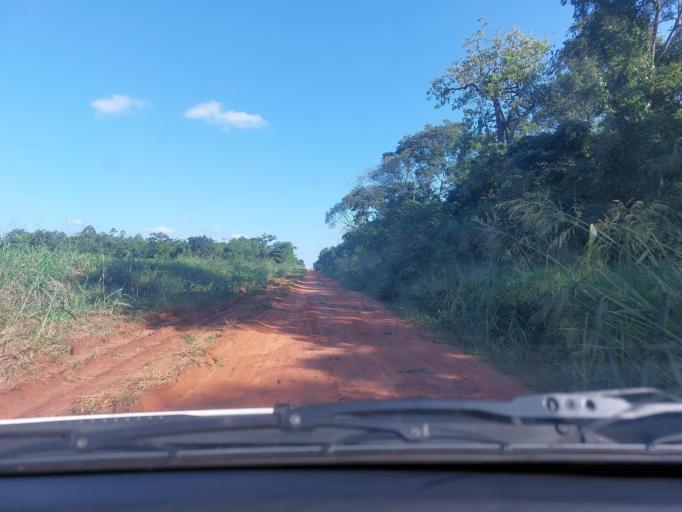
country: PY
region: San Pedro
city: Guayaybi
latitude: -24.5083
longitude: -56.5461
